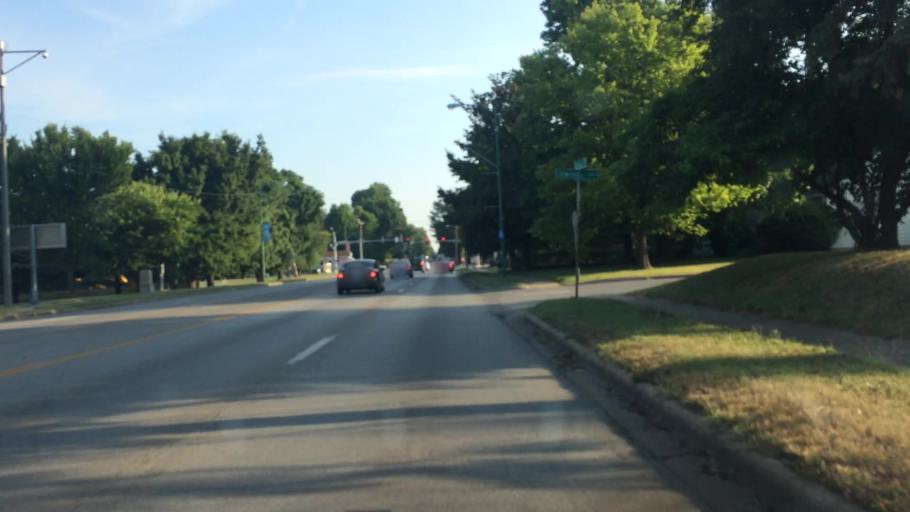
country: US
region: Missouri
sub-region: Greene County
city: Springfield
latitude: 37.1877
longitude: -93.2764
